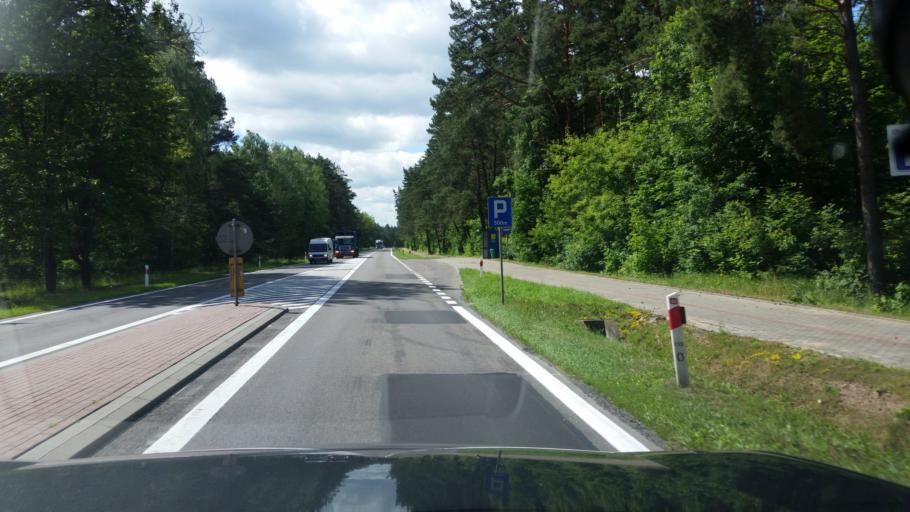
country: PL
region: Podlasie
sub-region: Powiat grajewski
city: Rajgrod
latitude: 53.7131
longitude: 22.6724
